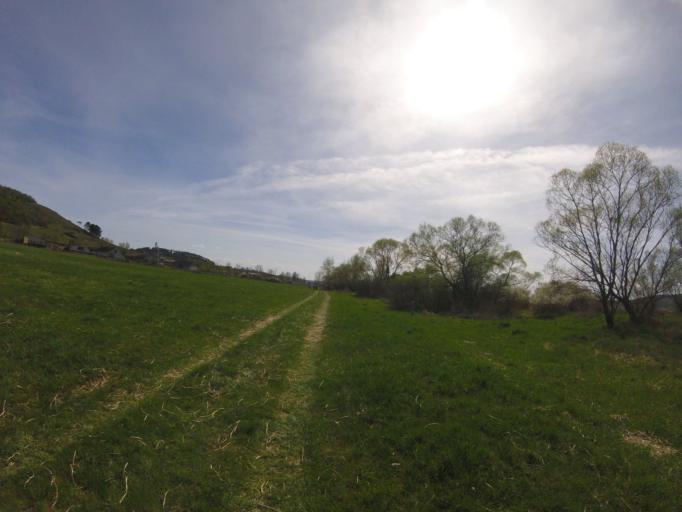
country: HU
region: Borsod-Abauj-Zemplen
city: Szendro
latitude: 48.4216
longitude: 20.7295
